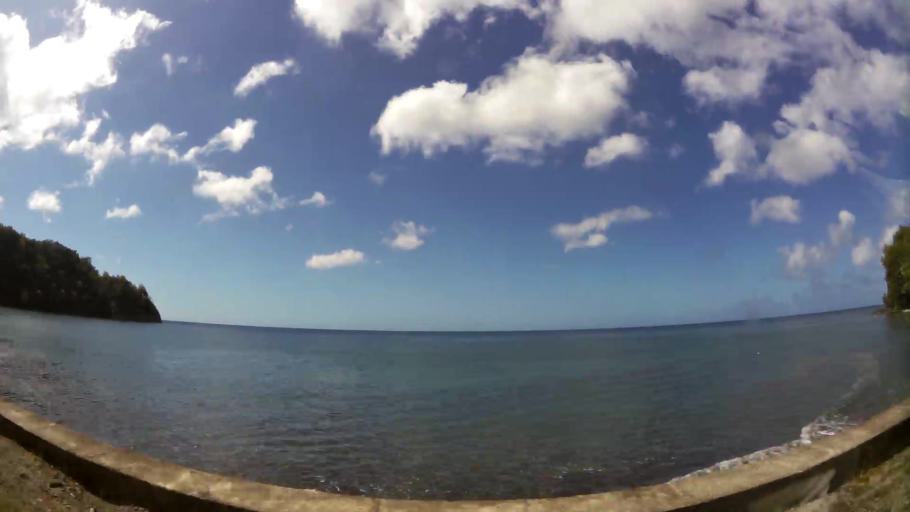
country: DM
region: Saint John
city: Portsmouth
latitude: 15.6114
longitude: -61.4646
